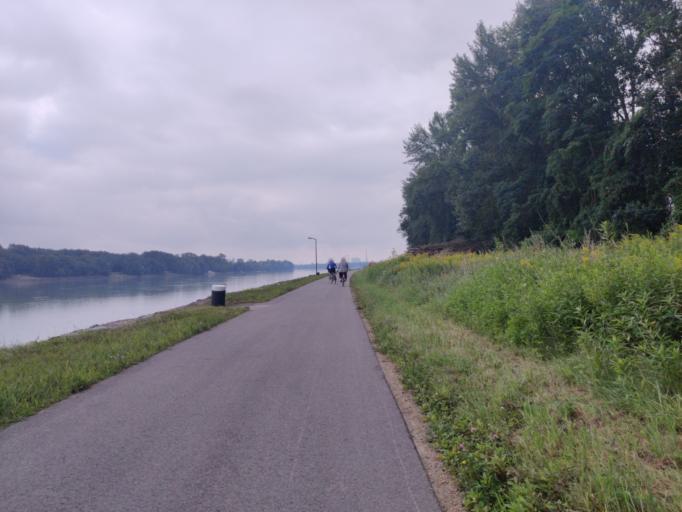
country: AT
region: Lower Austria
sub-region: Politischer Bezirk Tulln
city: Kirchberg am Wagram
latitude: 48.3677
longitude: 15.8738
